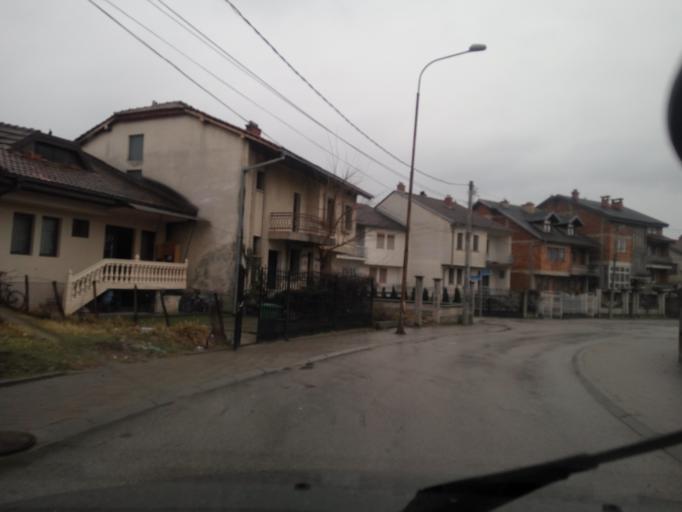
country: XK
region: Gjakova
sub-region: Komuna e Gjakoves
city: Gjakove
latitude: 42.3662
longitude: 20.4431
